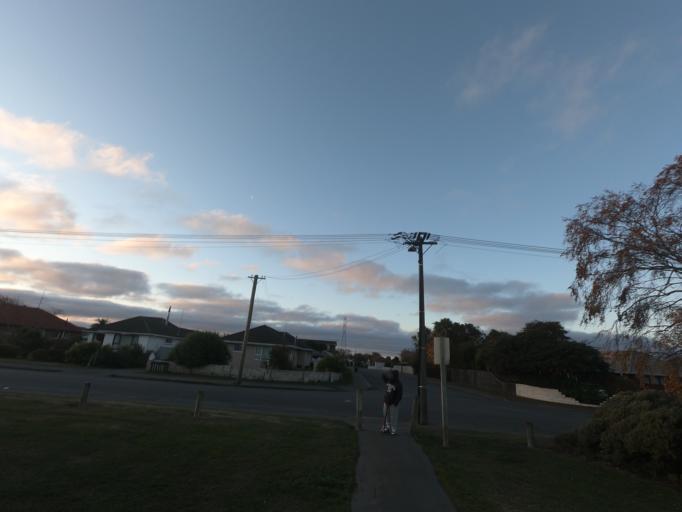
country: NZ
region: Canterbury
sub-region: Selwyn District
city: Prebbleton
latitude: -43.5747
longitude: 172.5626
